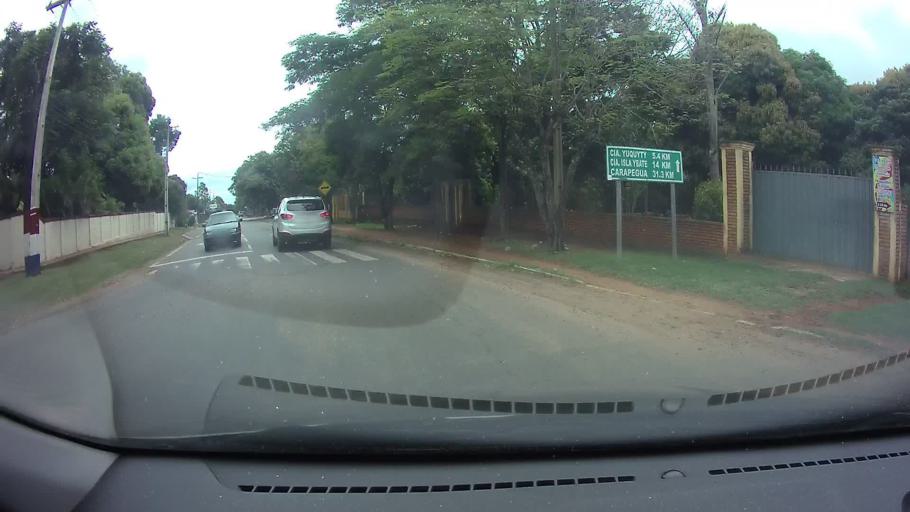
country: PY
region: Central
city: Nueva Italia
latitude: -25.6127
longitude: -57.4622
